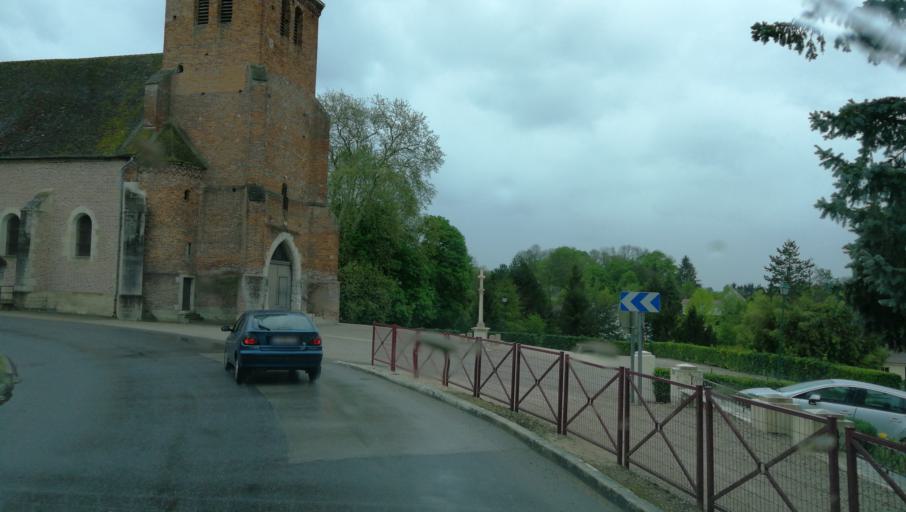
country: FR
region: Bourgogne
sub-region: Departement de Saone-et-Loire
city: Pierre-de-Bresse
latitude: 46.8871
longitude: 5.2576
